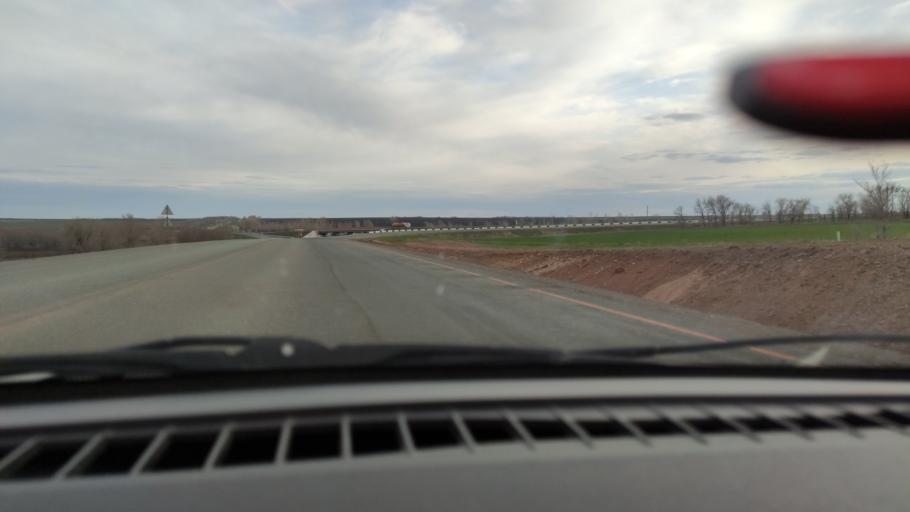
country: RU
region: Orenburg
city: Sakmara
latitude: 52.1797
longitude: 55.2918
